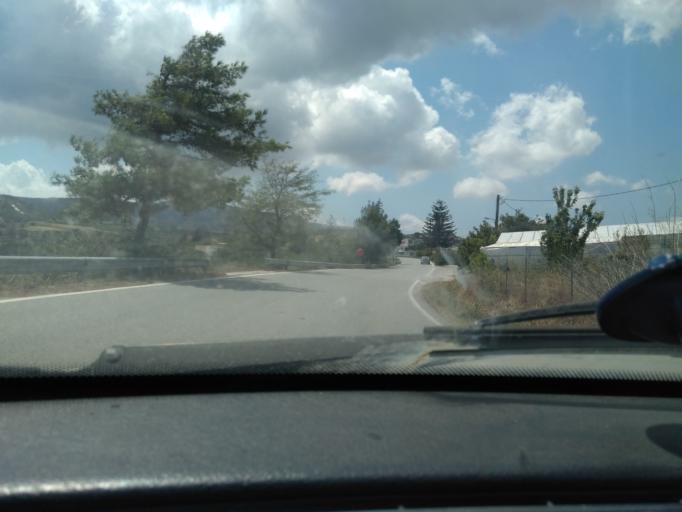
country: GR
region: Crete
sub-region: Nomos Lasithiou
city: Siteia
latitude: 35.1059
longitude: 26.0597
